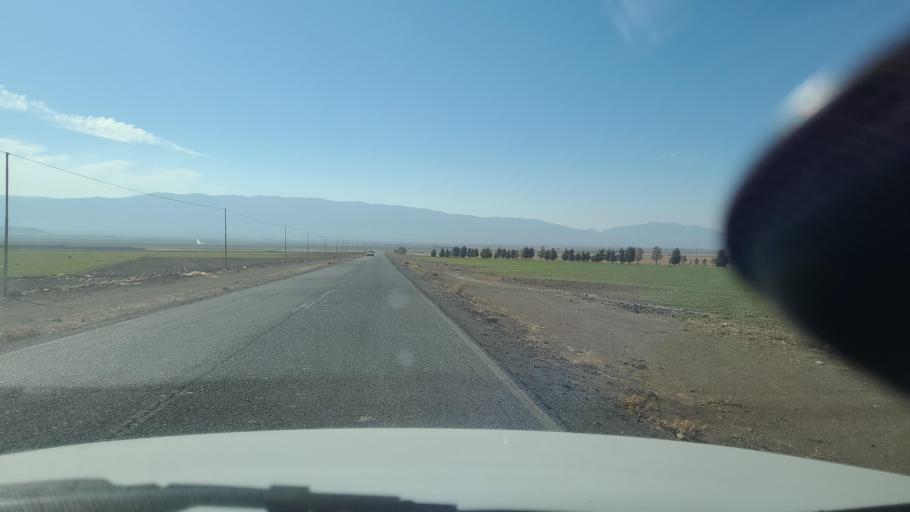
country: IR
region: Razavi Khorasan
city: Dowlatabad
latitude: 35.6057
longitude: 59.4645
